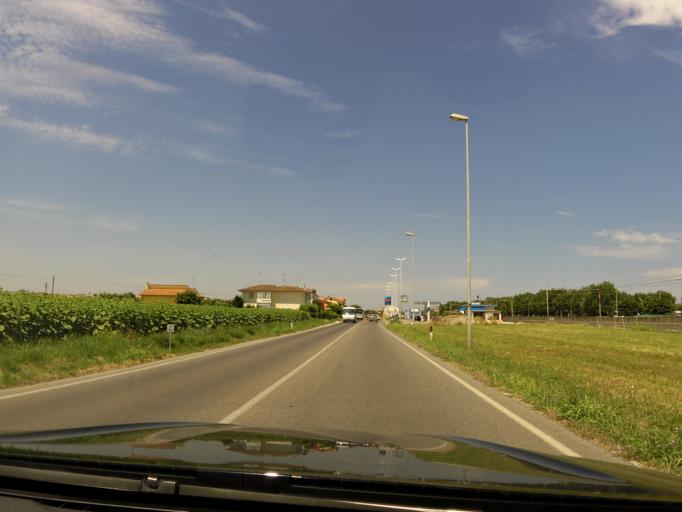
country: IT
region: The Marches
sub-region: Provincia di Pesaro e Urbino
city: Marotta
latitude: 43.7781
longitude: 13.1234
